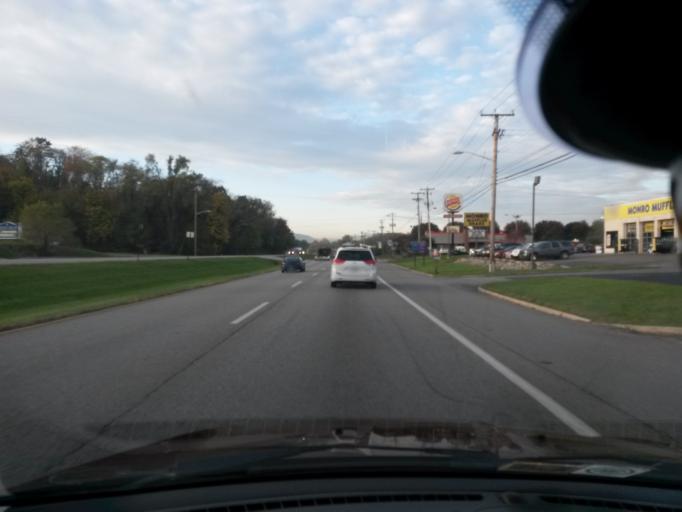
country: US
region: Virginia
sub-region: Roanoke County
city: Vinton
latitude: 37.3063
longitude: -79.8897
